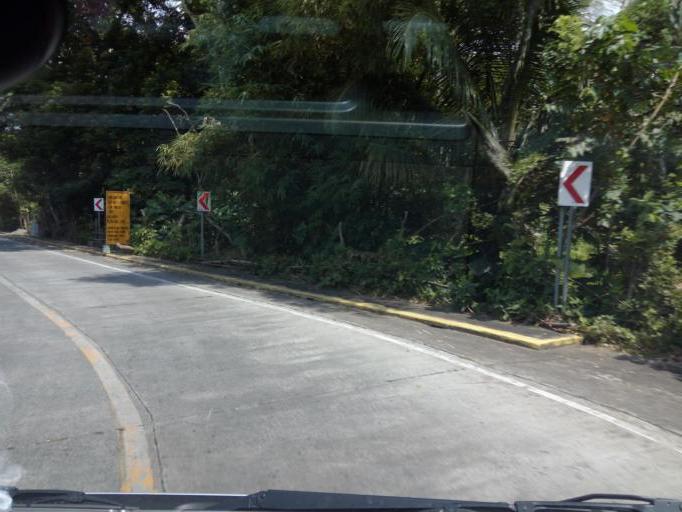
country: PH
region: Central Luzon
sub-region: Province of Aurora
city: Maria Aurora
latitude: 15.8009
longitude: 121.4744
